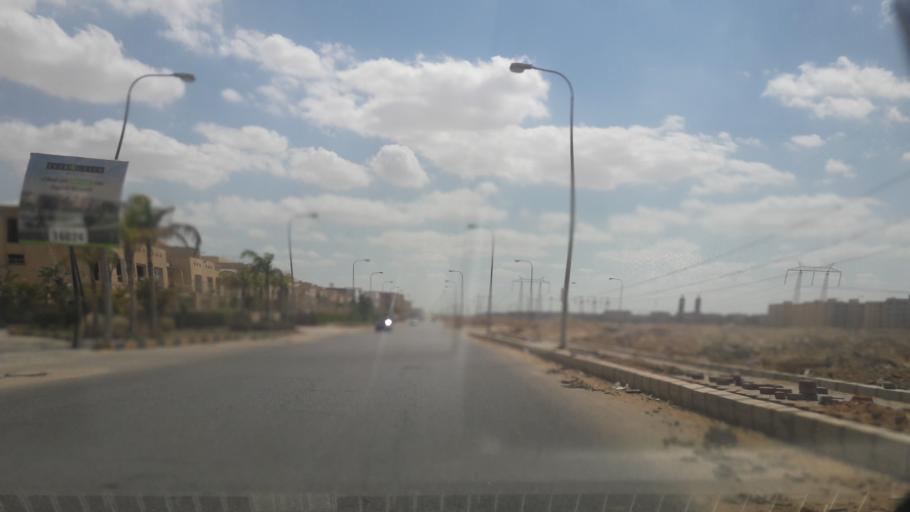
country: EG
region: Al Jizah
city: Madinat Sittah Uktubar
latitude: 29.9388
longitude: 31.0585
